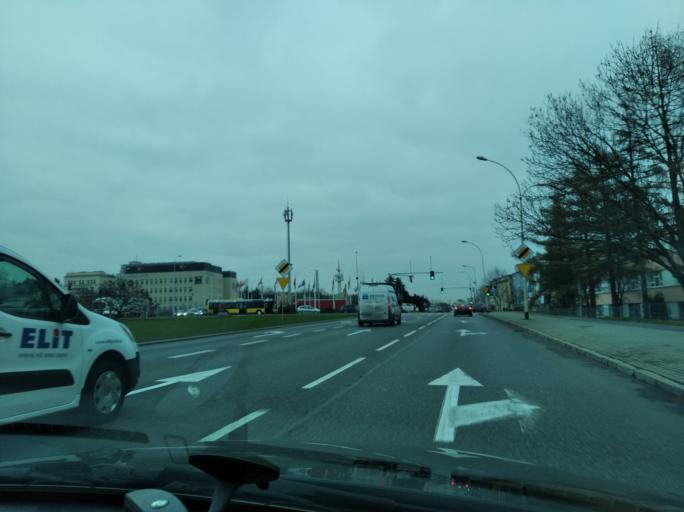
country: PL
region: Subcarpathian Voivodeship
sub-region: Rzeszow
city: Rzeszow
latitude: 50.0444
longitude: 21.9821
